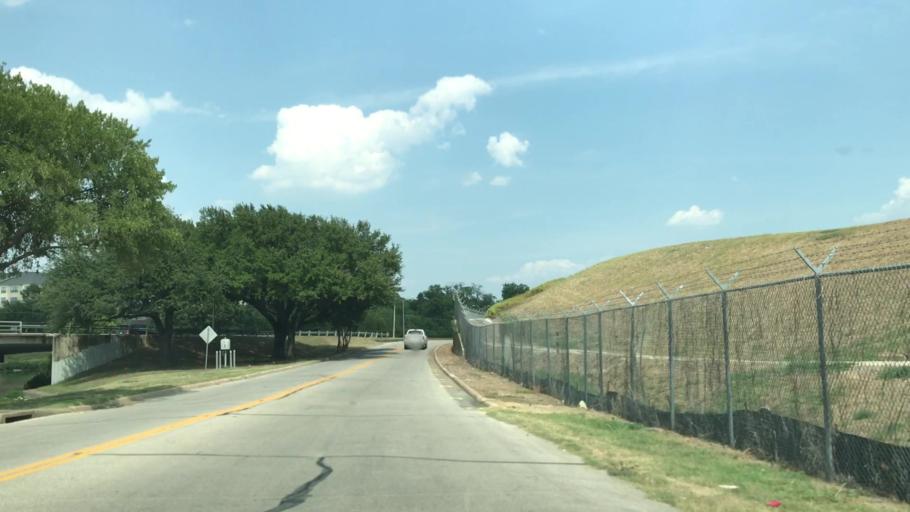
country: US
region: Texas
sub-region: Dallas County
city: University Park
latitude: 32.8593
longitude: -96.8547
